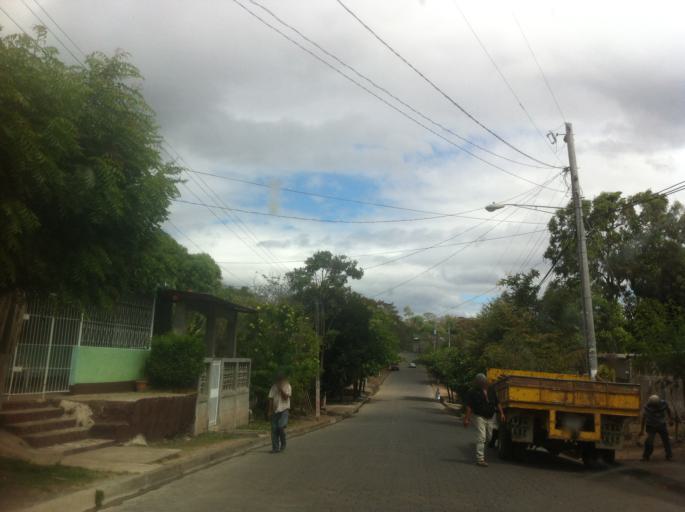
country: NI
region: Chontales
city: Juigalpa
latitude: 12.0942
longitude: -85.3601
